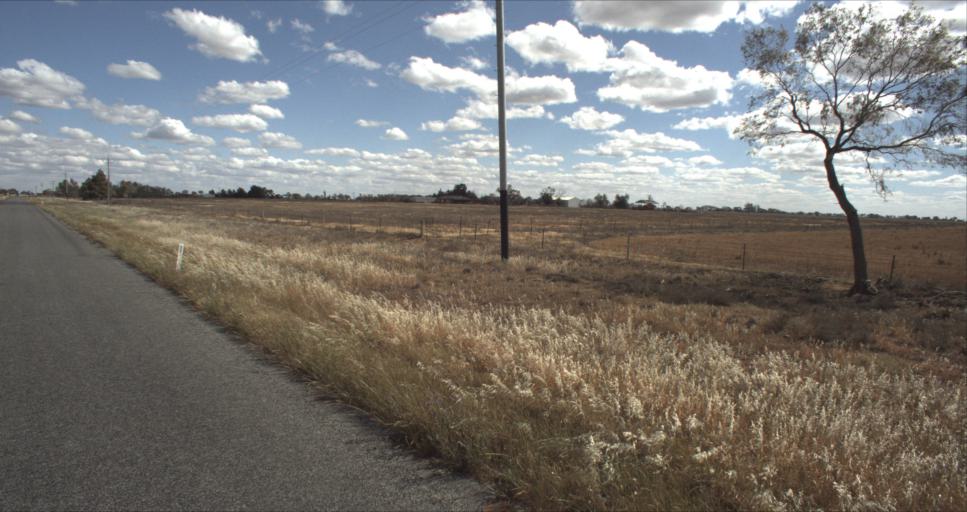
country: AU
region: New South Wales
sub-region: Leeton
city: Leeton
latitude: -34.4548
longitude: 146.2539
